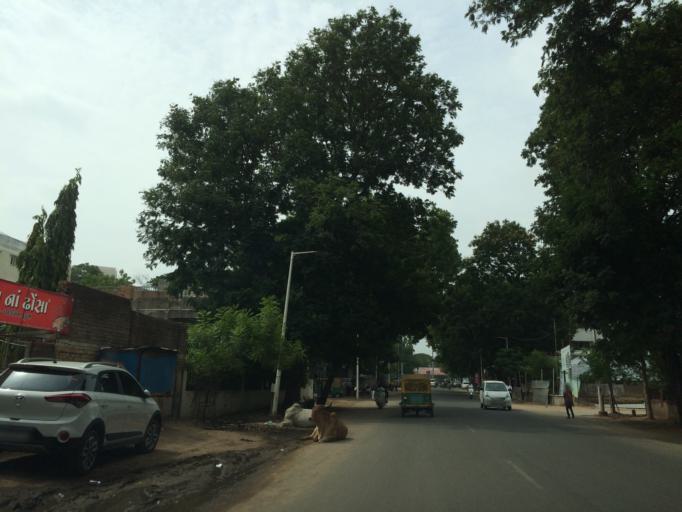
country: IN
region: Gujarat
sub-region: Anand
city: Karamsad
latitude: 22.5482
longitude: 72.9291
